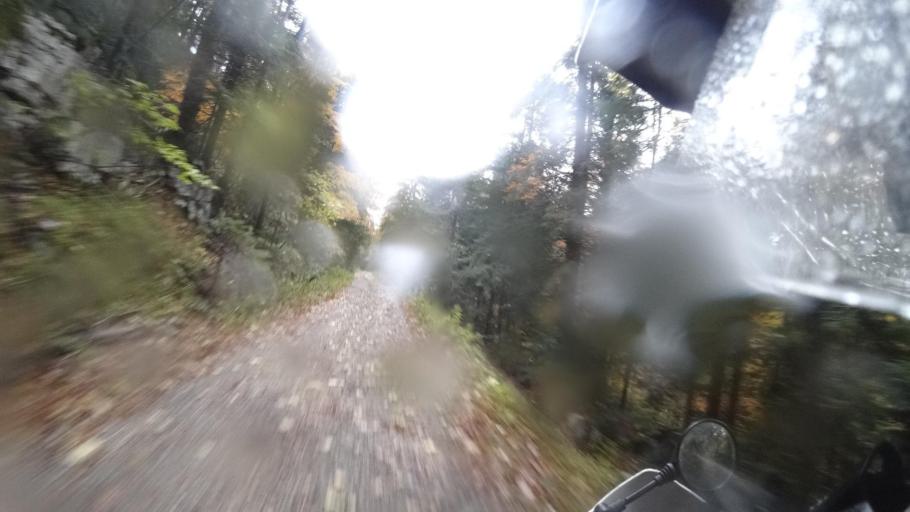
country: HR
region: Primorsko-Goranska
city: Vrbovsko
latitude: 45.3017
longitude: 14.9926
